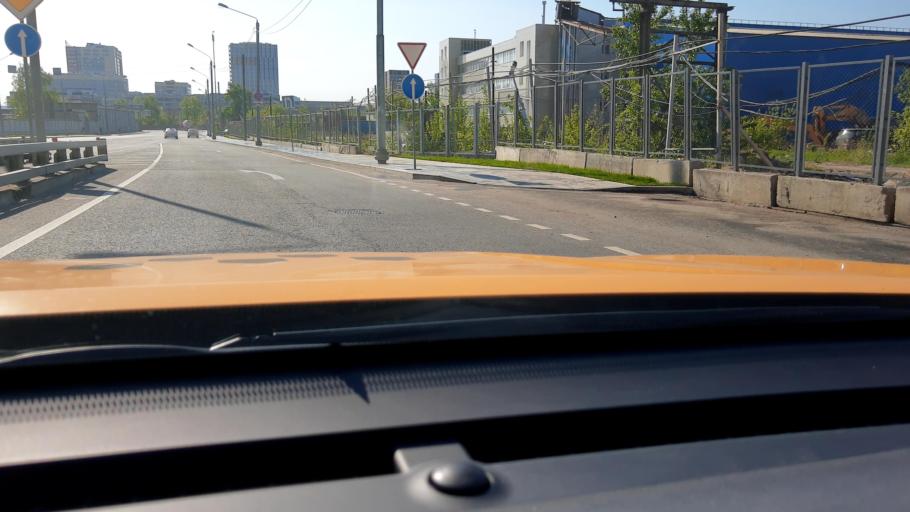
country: RU
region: Moskovskaya
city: Kozhukhovo
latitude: 55.6965
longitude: 37.6524
